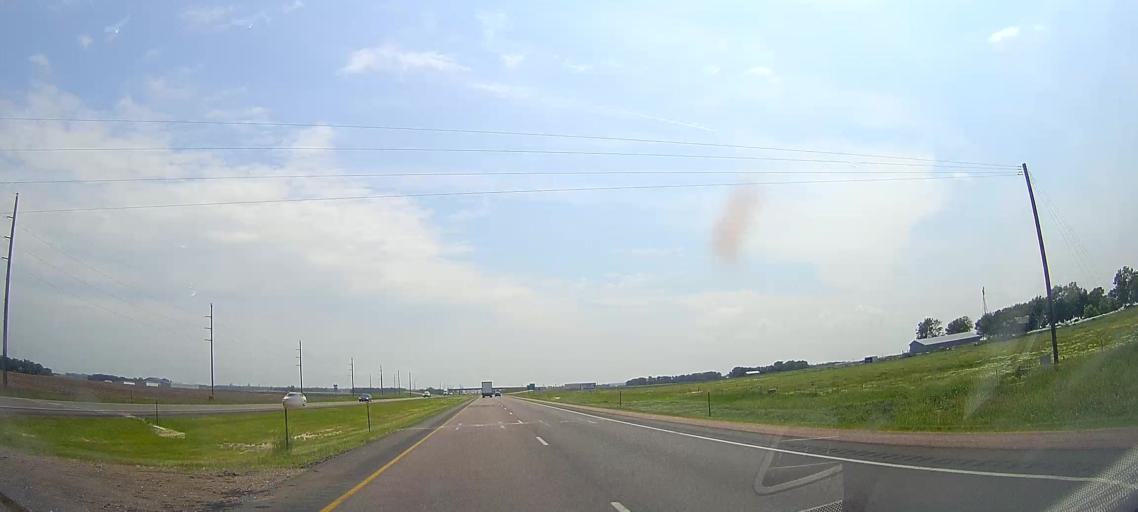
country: US
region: South Dakota
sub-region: Union County
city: Beresford
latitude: 43.1343
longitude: -96.7968
